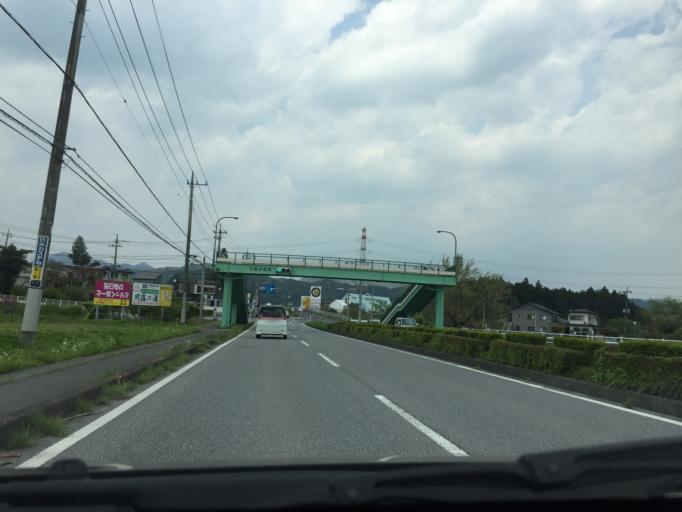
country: JP
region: Tochigi
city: Imaichi
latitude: 36.7616
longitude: 139.7165
